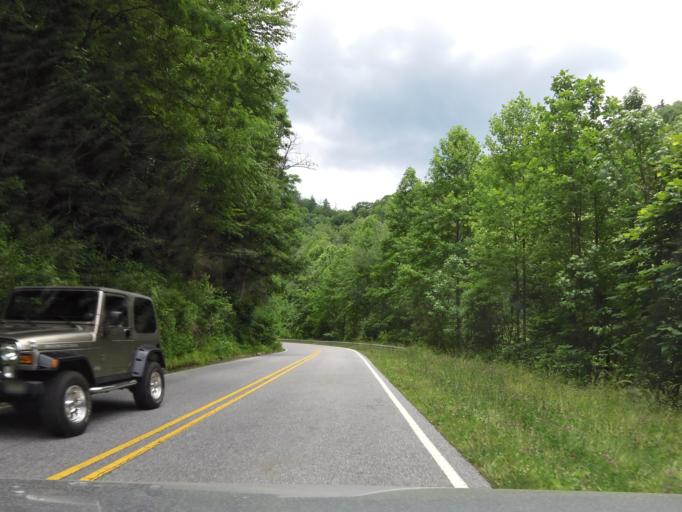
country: US
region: North Carolina
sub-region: Graham County
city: Robbinsville
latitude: 35.4228
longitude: -83.8947
